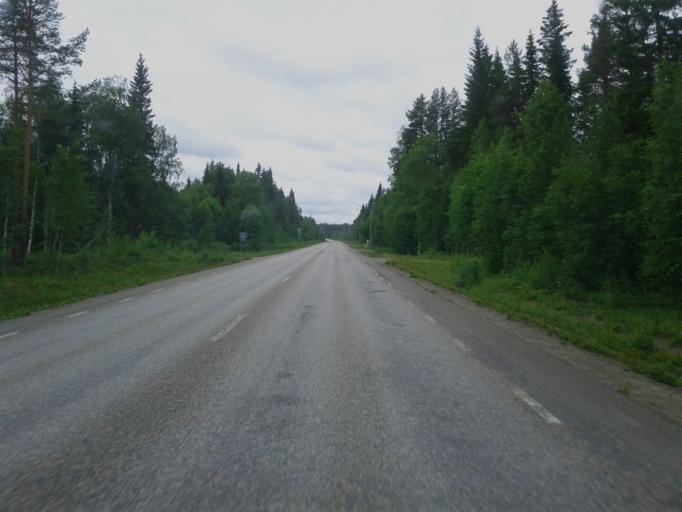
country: SE
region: Vaesterbotten
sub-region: Skelleftea Kommun
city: Langsele
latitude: 64.9620
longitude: 19.8810
